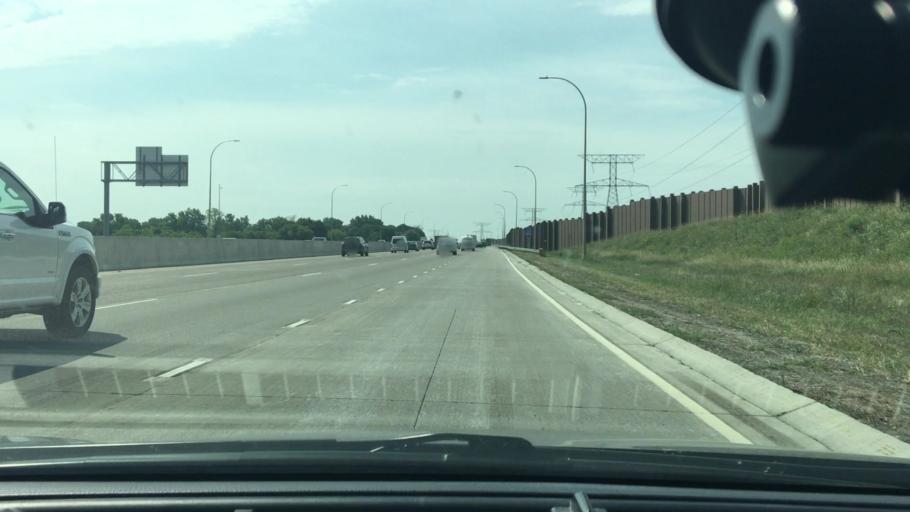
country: US
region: Minnesota
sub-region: Hennepin County
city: Maple Grove
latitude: 45.0639
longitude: -93.4492
